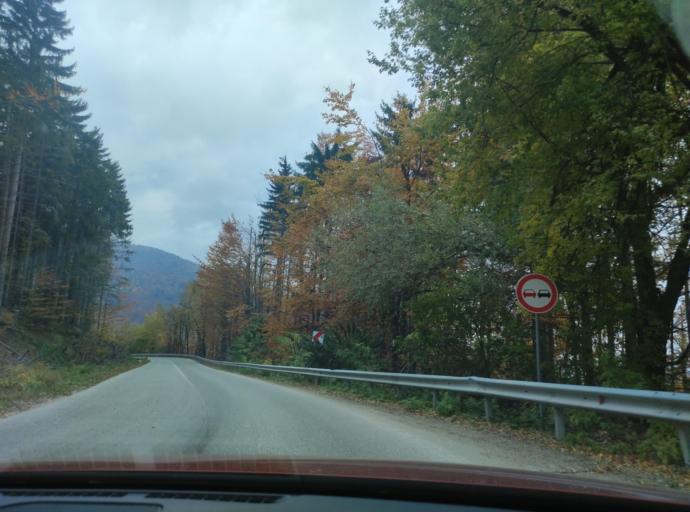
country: BG
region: Montana
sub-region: Obshtina Berkovitsa
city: Berkovitsa
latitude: 43.1470
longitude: 23.1512
